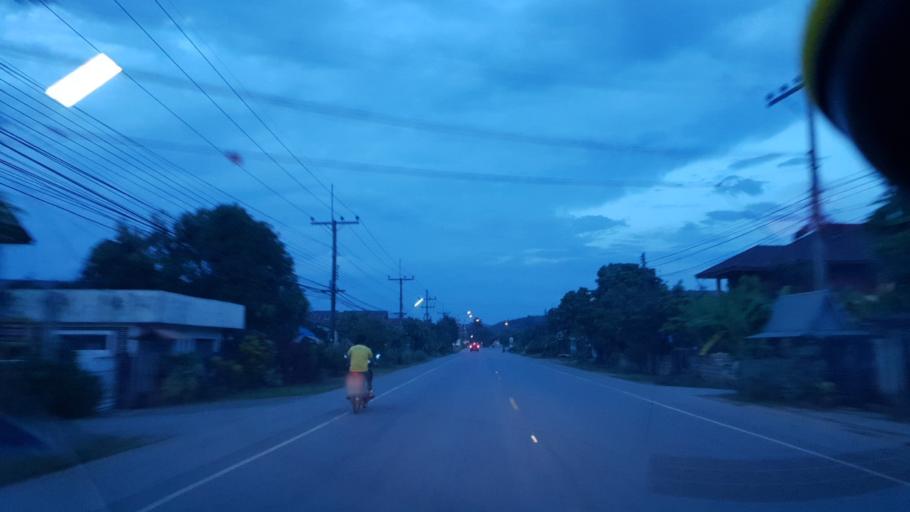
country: TH
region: Chiang Rai
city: Wiang Chiang Rung
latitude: 19.9845
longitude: 100.0261
